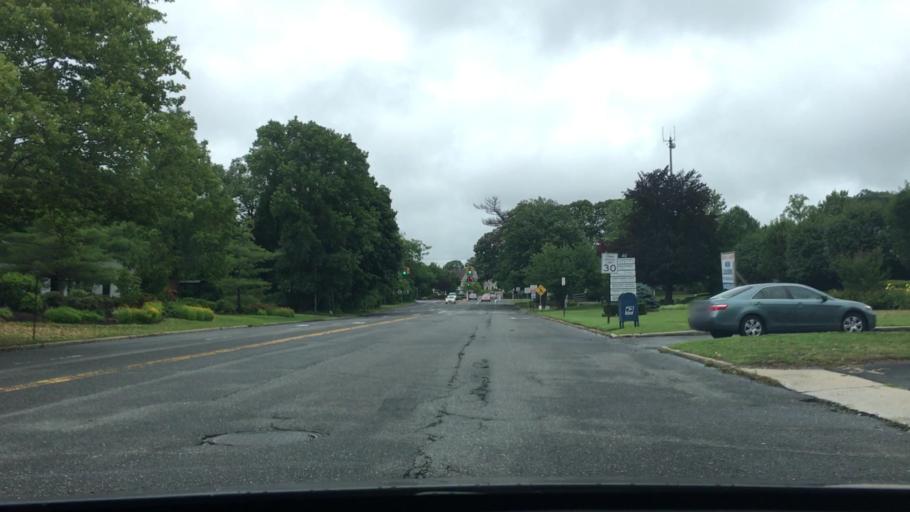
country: US
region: New York
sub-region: Nassau County
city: Syosset
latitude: 40.8106
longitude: -73.4862
